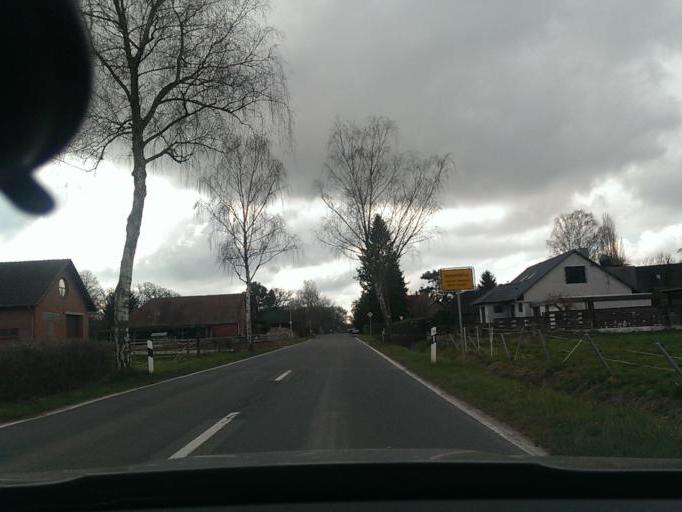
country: DE
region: Lower Saxony
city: Elze
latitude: 52.5763
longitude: 9.7140
